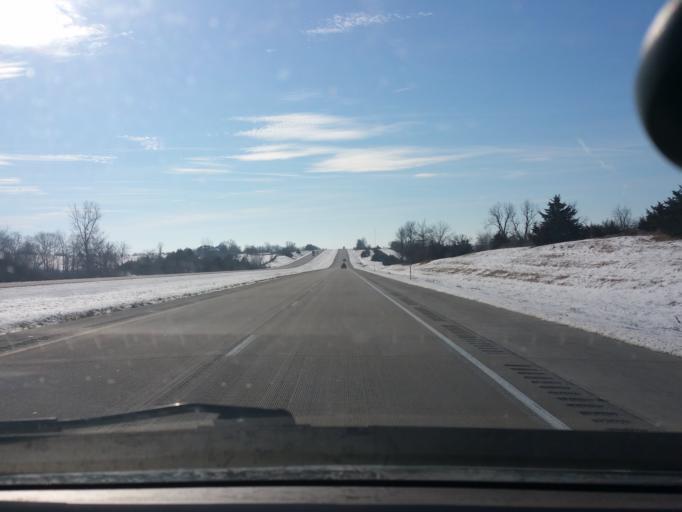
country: US
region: Iowa
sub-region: Decatur County
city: Leon
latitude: 40.7919
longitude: -93.8349
